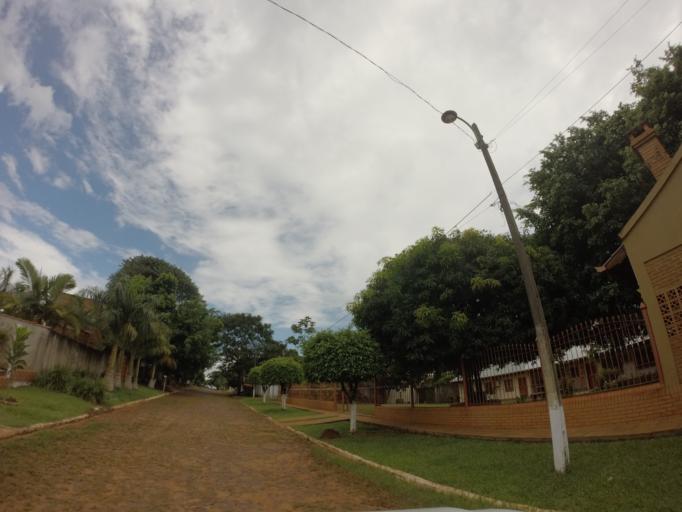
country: PY
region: Alto Parana
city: Ciudad del Este
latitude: -25.4147
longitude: -54.6312
